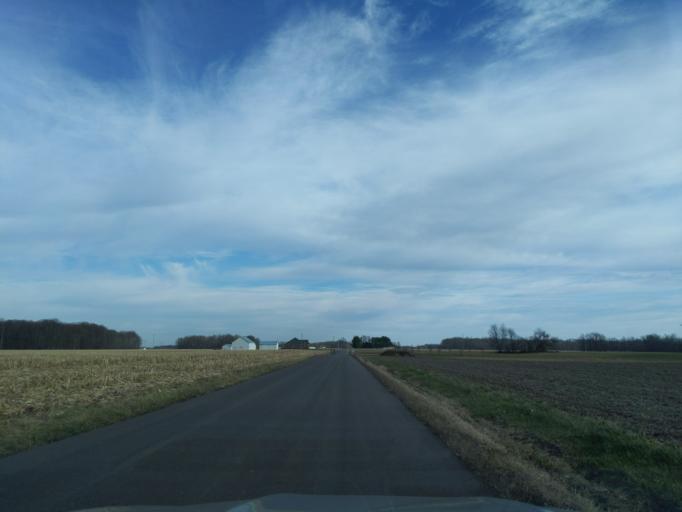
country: US
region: Indiana
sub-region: Decatur County
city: Greensburg
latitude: 39.2343
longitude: -85.4243
